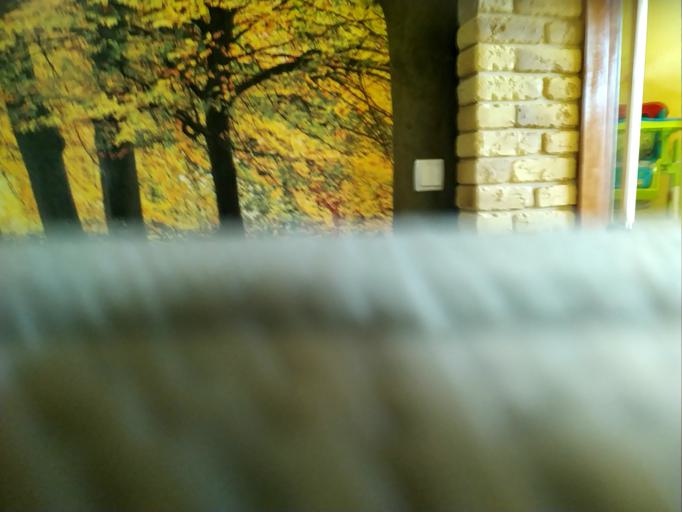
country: RU
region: Vologda
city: Nelazskoye
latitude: 59.4536
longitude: 37.6065
